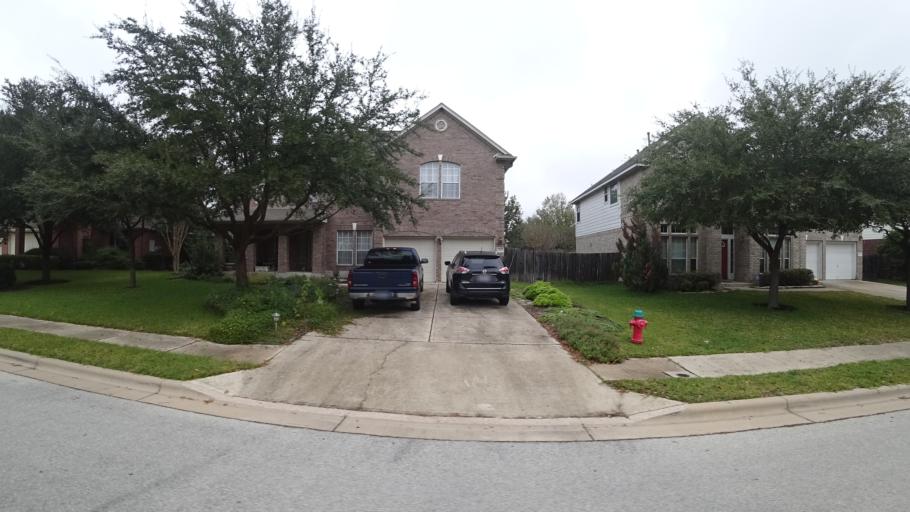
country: US
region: Texas
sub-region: Travis County
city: Pflugerville
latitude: 30.4286
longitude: -97.6179
